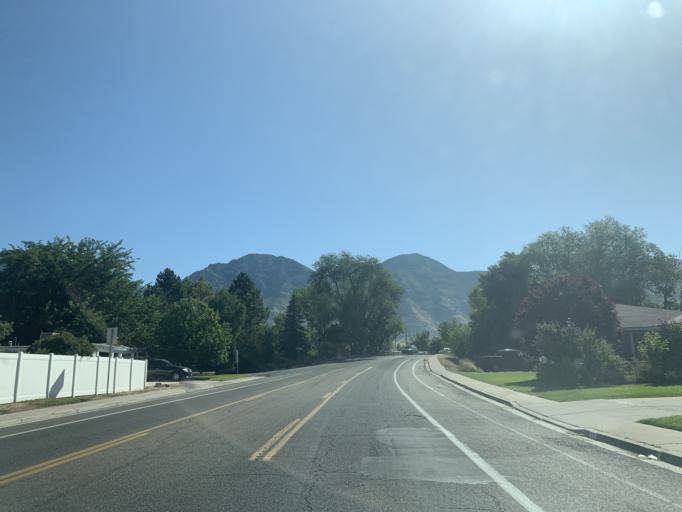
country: US
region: Utah
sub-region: Utah County
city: Provo
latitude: 40.2449
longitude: -111.6751
